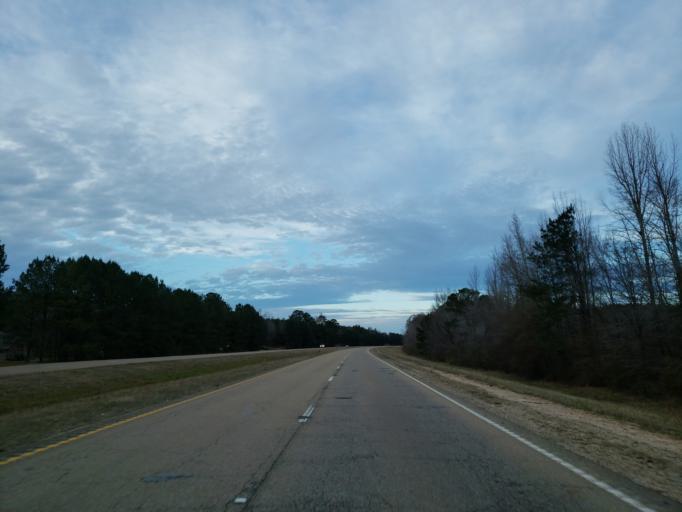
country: US
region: Mississippi
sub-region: Lauderdale County
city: Meridian Station
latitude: 32.5891
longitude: -88.5015
